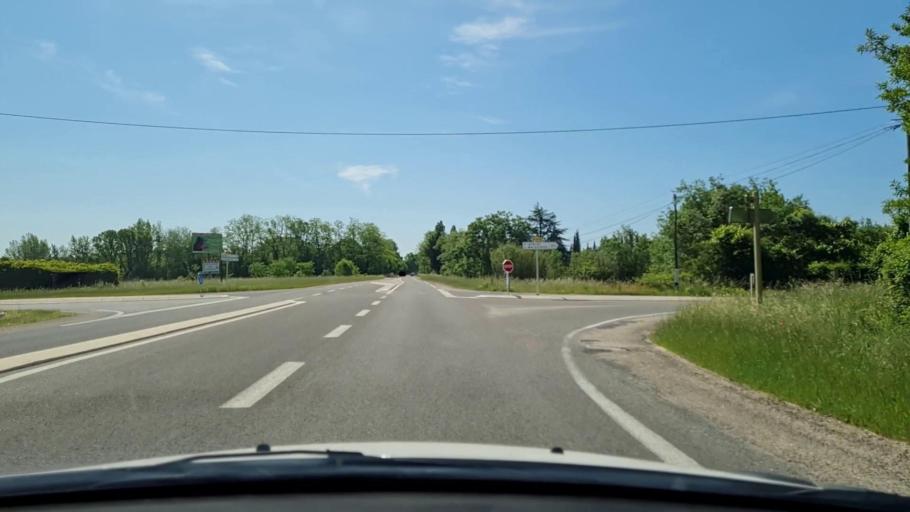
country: FR
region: Languedoc-Roussillon
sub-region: Departement du Gard
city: Saint-Genies-de-Malgoires
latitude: 43.9571
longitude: 4.2412
